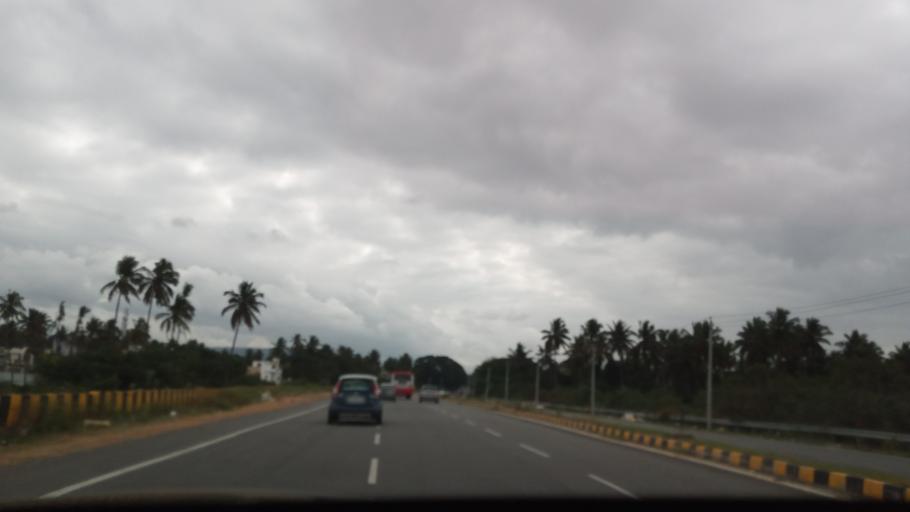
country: IN
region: Karnataka
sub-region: Mysore
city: Mysore
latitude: 12.3419
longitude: 76.6580
